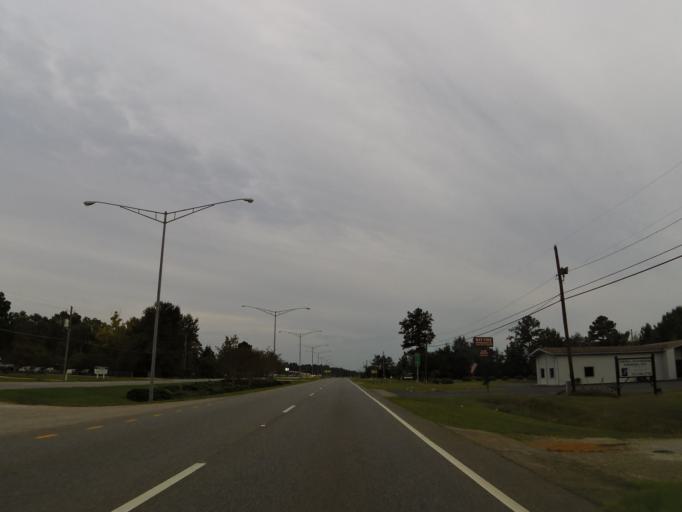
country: US
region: Alabama
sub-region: Baldwin County
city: Bay Minette
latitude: 30.8444
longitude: -87.7756
